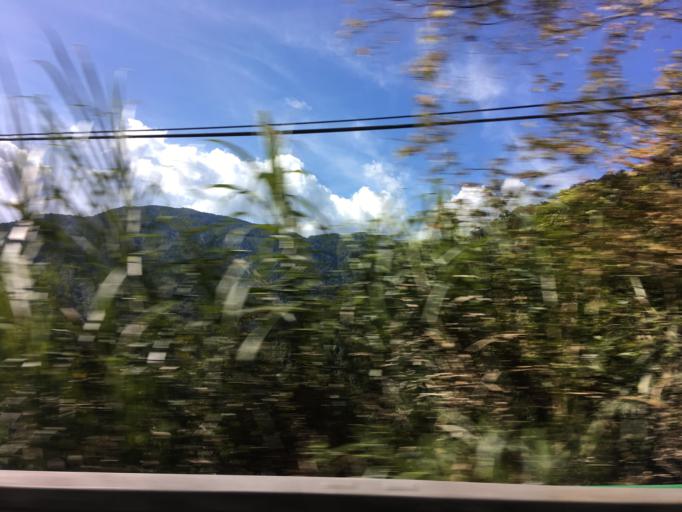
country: TW
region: Taiwan
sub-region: Yilan
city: Yilan
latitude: 24.5555
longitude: 121.5049
